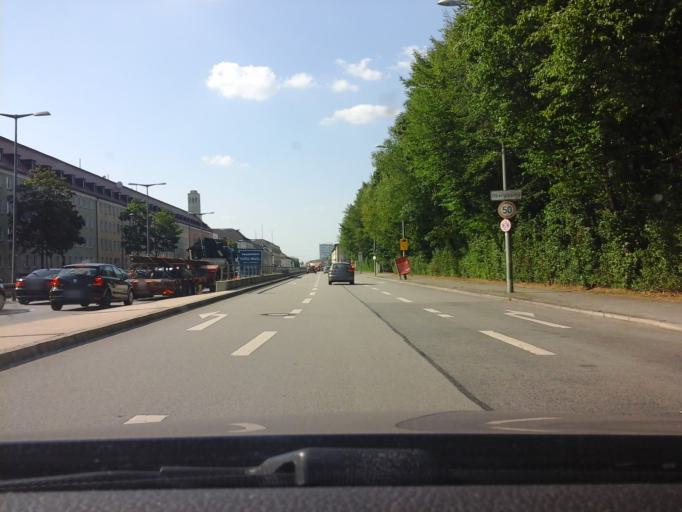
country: DE
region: Bavaria
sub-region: Upper Bavaria
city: Munich
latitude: 48.0974
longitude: 11.5868
